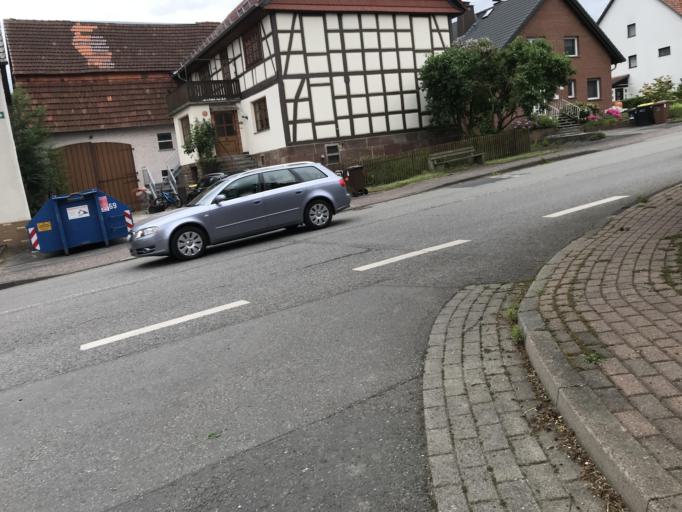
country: DE
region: Hesse
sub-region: Regierungsbezirk Kassel
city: Martinhagen
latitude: 51.2862
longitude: 9.2871
